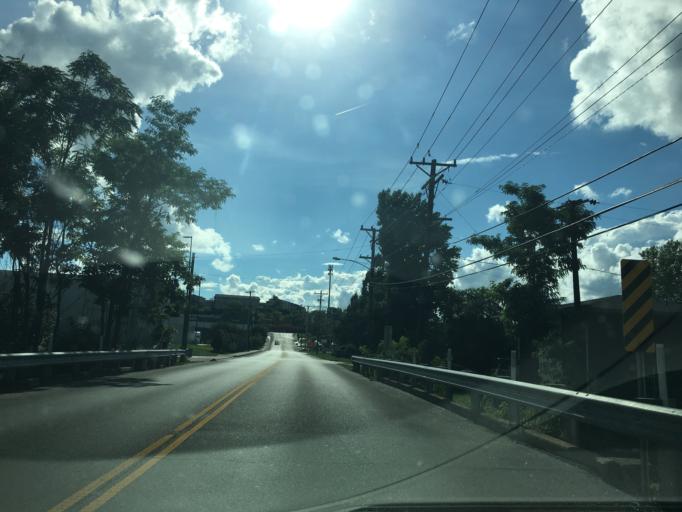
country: US
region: Tennessee
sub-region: Davidson County
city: Oak Hill
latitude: 36.0831
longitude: -86.7238
